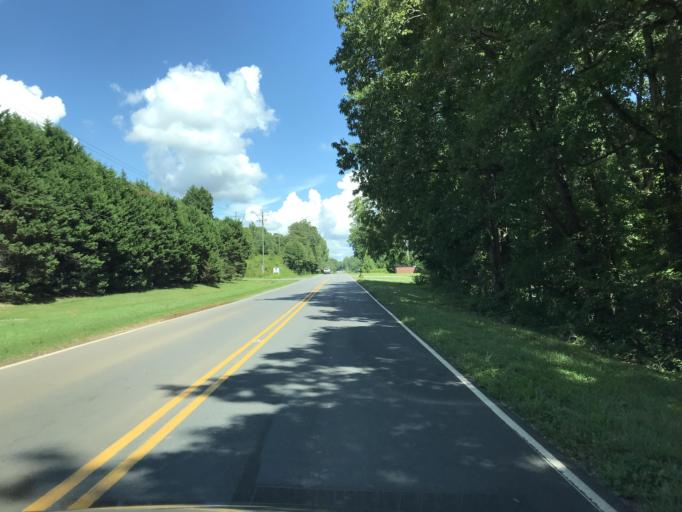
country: US
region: North Carolina
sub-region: Catawba County
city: Lake Norman of Catawba
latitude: 35.5731
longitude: -81.0209
